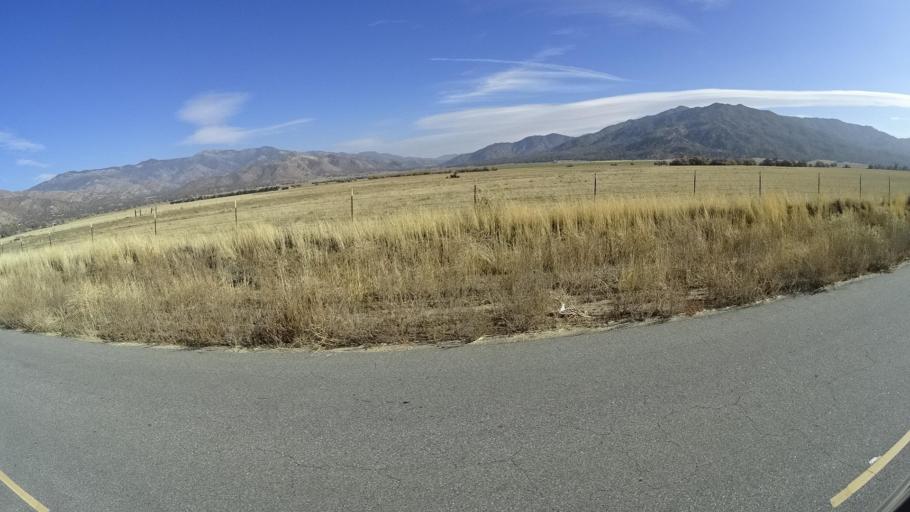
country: US
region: California
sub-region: Kern County
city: Bodfish
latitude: 35.4093
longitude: -118.5463
